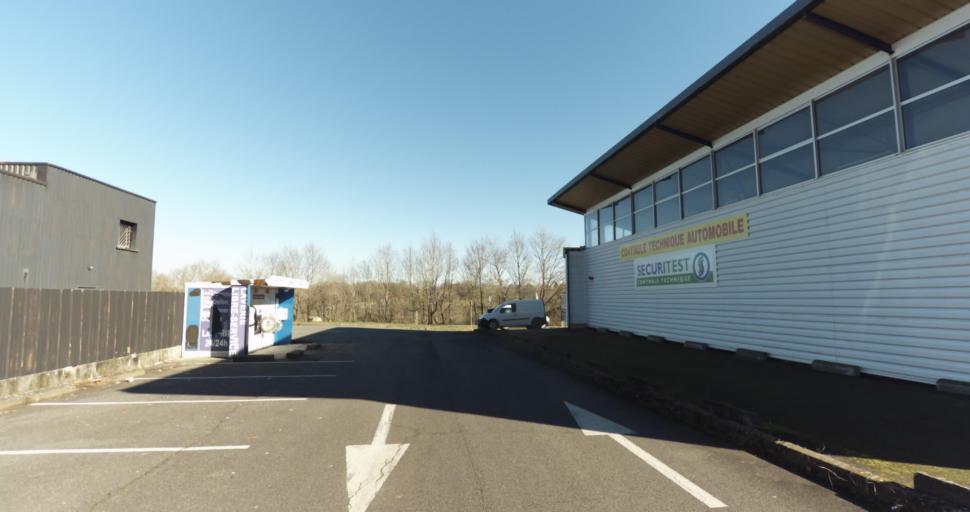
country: FR
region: Aquitaine
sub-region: Departement des Pyrenees-Atlantiques
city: Morlaas
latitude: 43.3480
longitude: -0.2556
